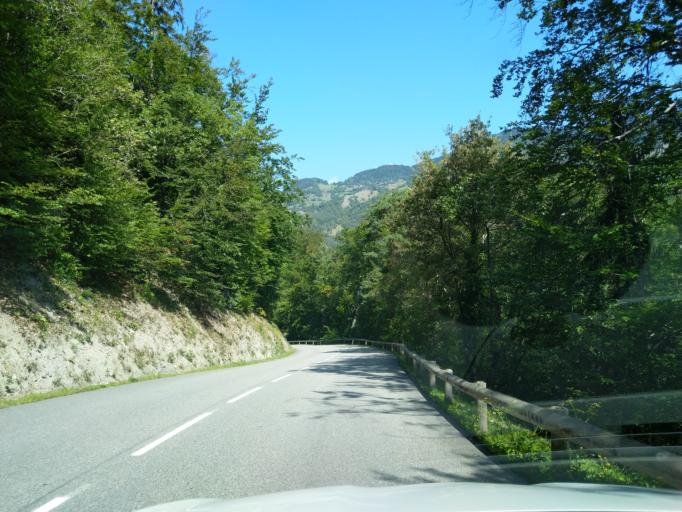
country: FR
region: Rhone-Alpes
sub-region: Departement de la Savoie
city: Les Allues
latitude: 45.4474
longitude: 6.5630
